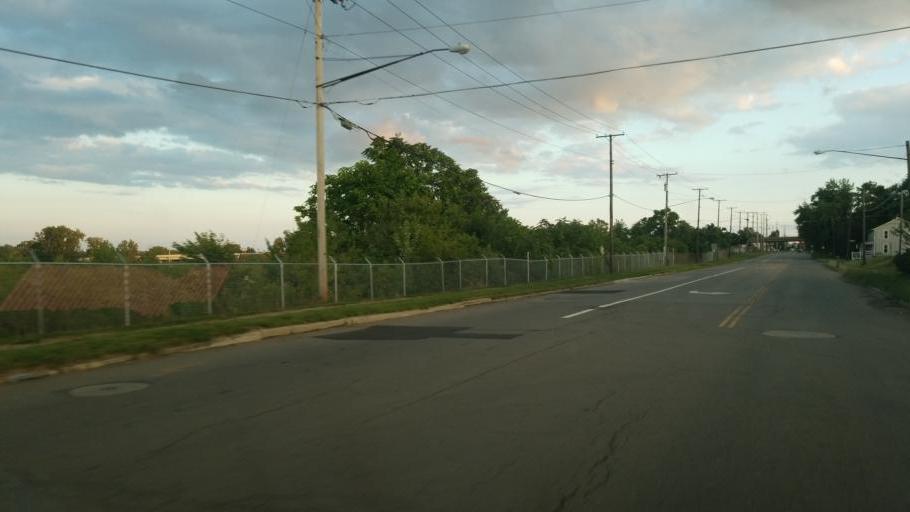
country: US
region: Ohio
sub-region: Richland County
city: Mansfield
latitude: 40.7813
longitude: -82.5230
